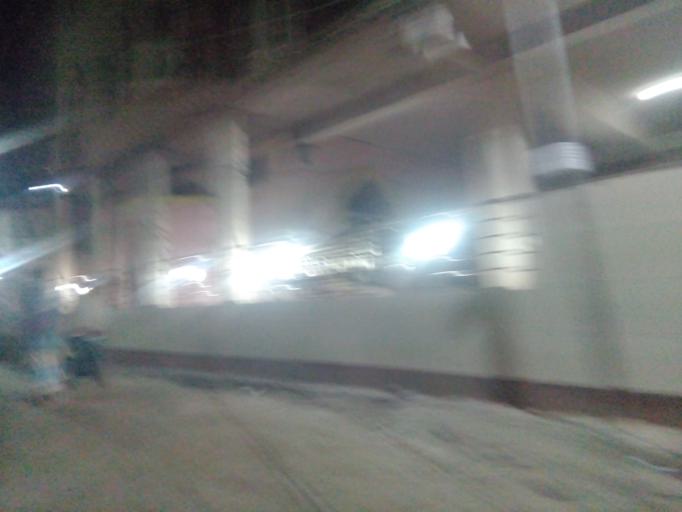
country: BD
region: Dhaka
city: Paltan
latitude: 23.7435
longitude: 90.4181
